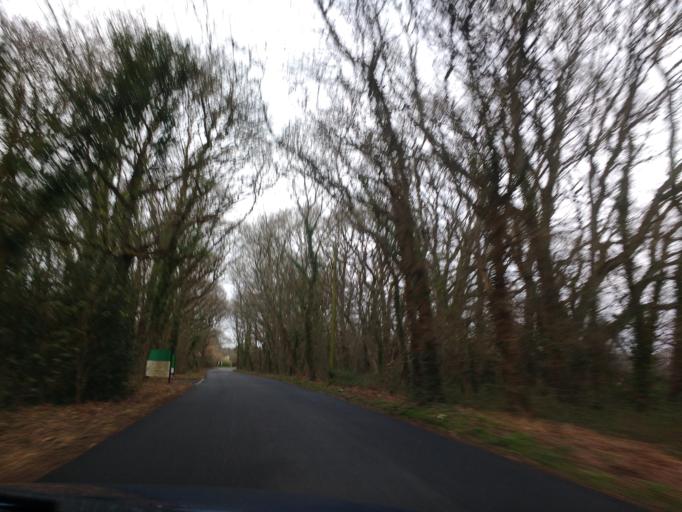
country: GB
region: England
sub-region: Isle of Wight
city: Shalfleet
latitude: 50.7141
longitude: -1.3725
